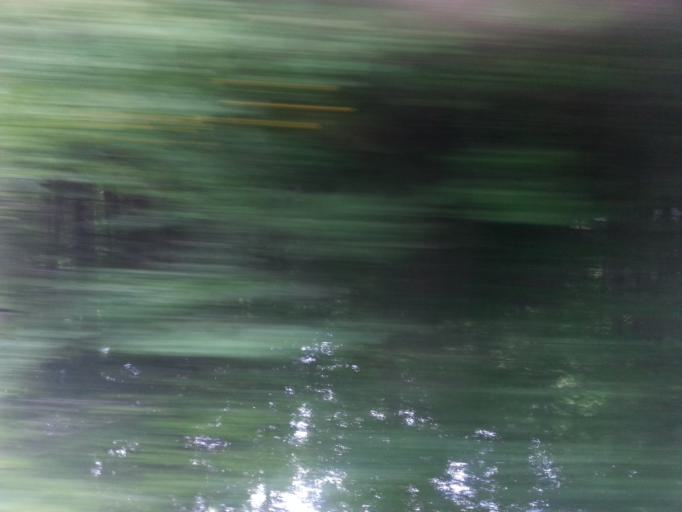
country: US
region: Tennessee
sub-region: Anderson County
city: Rocky Top
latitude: 36.1695
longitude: -84.2690
